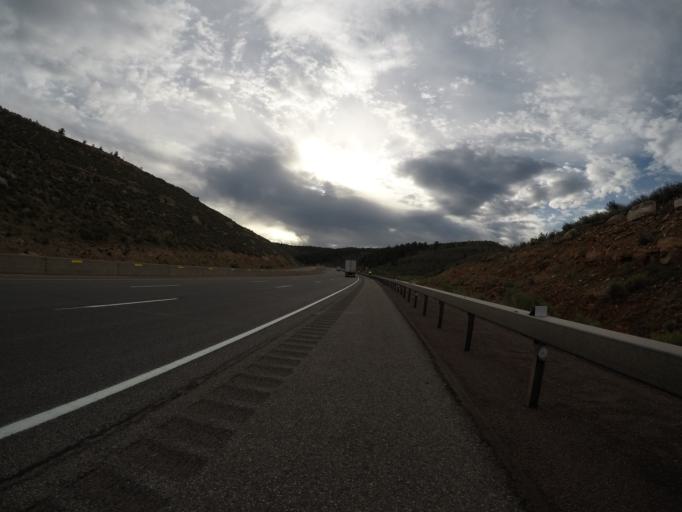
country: US
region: Wyoming
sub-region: Albany County
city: Laramie
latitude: 41.2716
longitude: -105.4916
